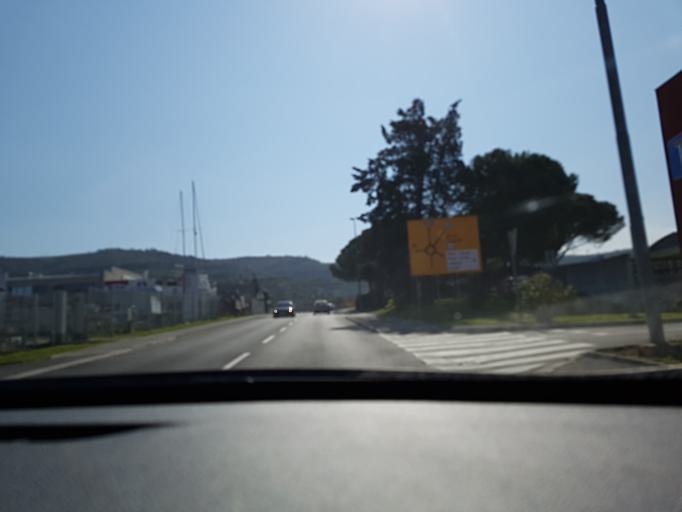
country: SI
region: Izola-Isola
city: Izola
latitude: 45.5369
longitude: 13.6707
